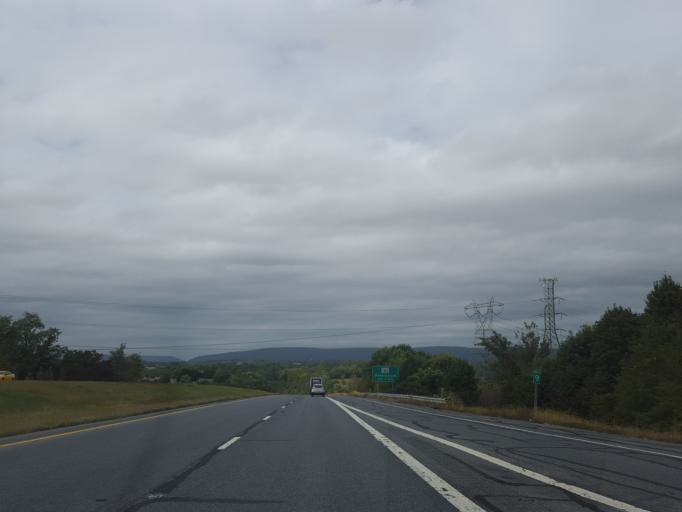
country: US
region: Maryland
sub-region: Frederick County
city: Jefferson
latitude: 39.3572
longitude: -77.5601
